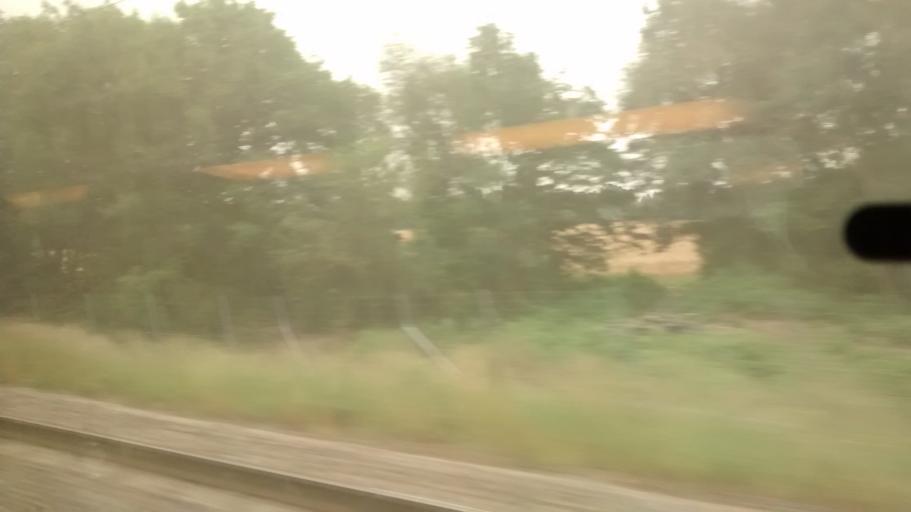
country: FR
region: Ile-de-France
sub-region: Departement de Seine-et-Marne
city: Le Chatelet-en-Brie
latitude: 48.5364
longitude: 2.7970
